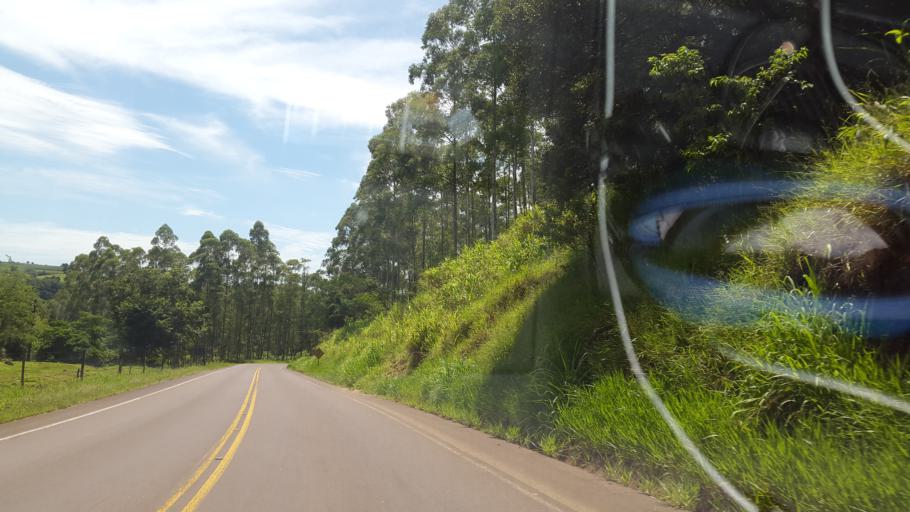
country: BR
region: Rio Grande do Sul
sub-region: Frederico Westphalen
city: Frederico Westphalen
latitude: -27.0665
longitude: -53.4664
